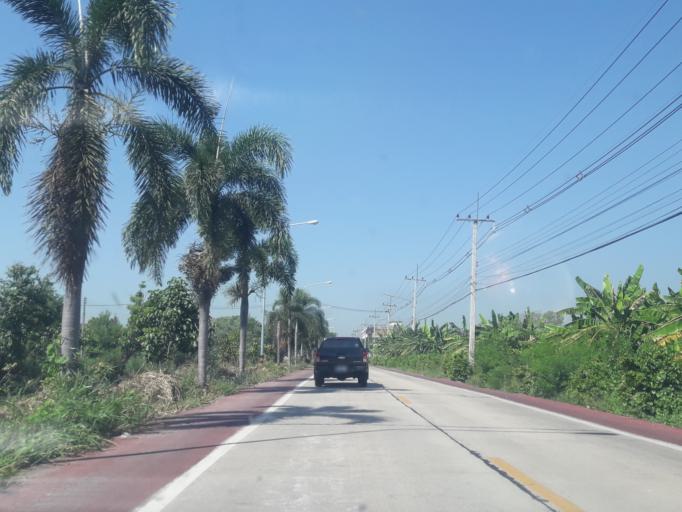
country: TH
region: Pathum Thani
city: Nong Suea
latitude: 14.1366
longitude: 100.8496
